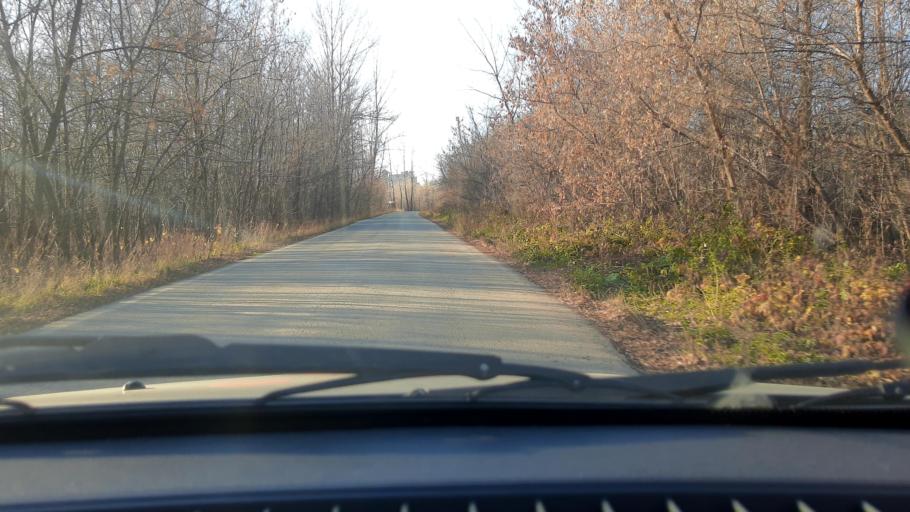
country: RU
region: Bashkortostan
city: Ufa
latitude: 54.6635
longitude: 55.9659
